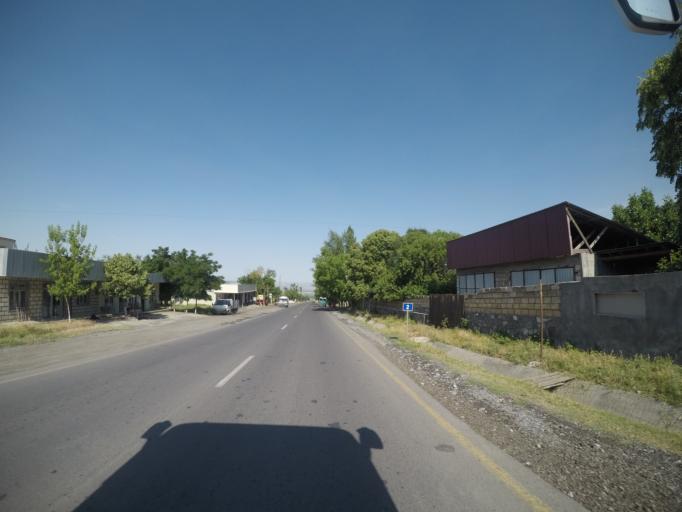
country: AZ
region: Shaki City
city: Sheki
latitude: 41.2103
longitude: 47.1424
